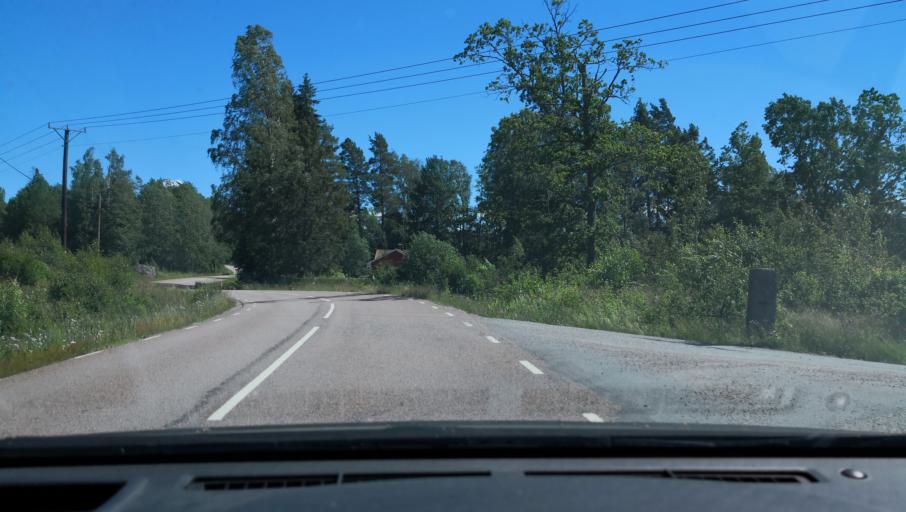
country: SE
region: Vaestmanland
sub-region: Arboga Kommun
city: Tyringe
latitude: 59.3003
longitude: 16.0202
